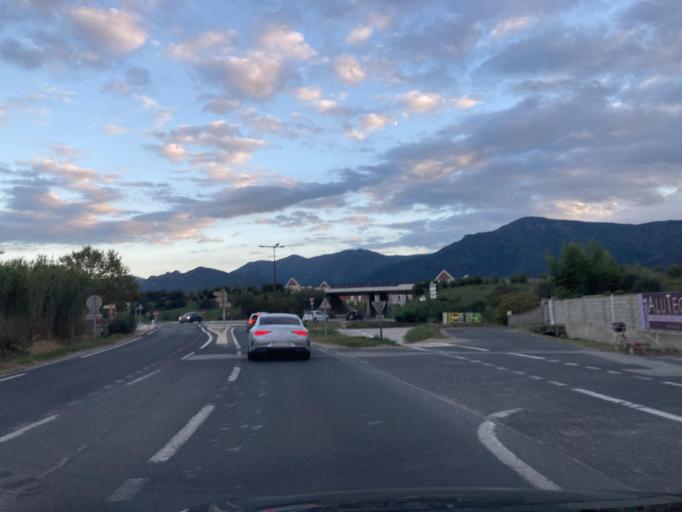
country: FR
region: Languedoc-Roussillon
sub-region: Departement des Pyrenees-Orientales
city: Sant Genis de Fontanes
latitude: 42.5495
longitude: 2.9176
